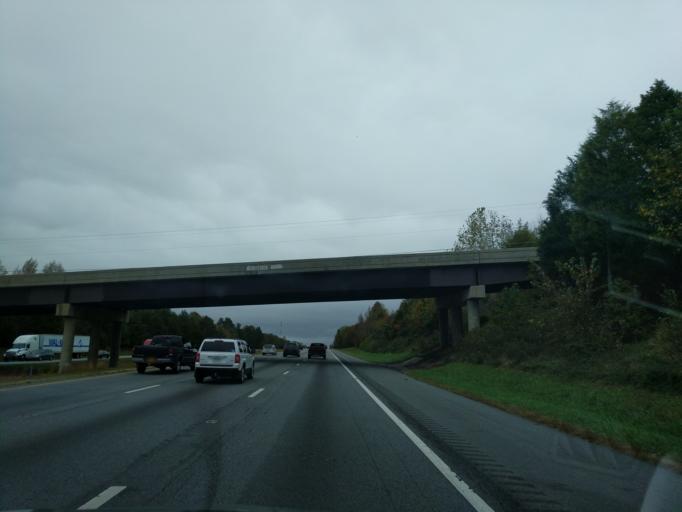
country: US
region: North Carolina
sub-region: Randolph County
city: Trinity
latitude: 35.8864
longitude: -79.9912
